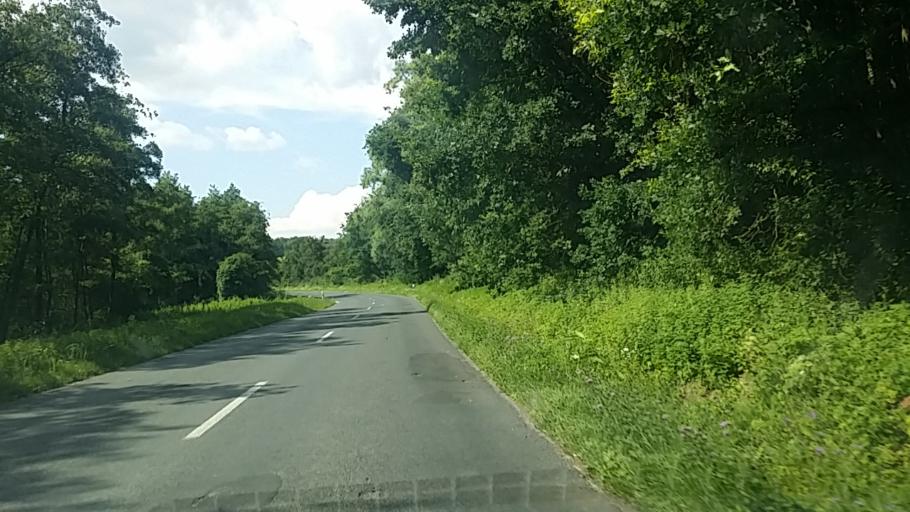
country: HU
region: Zala
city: Becsehely
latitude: 46.4842
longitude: 16.7919
